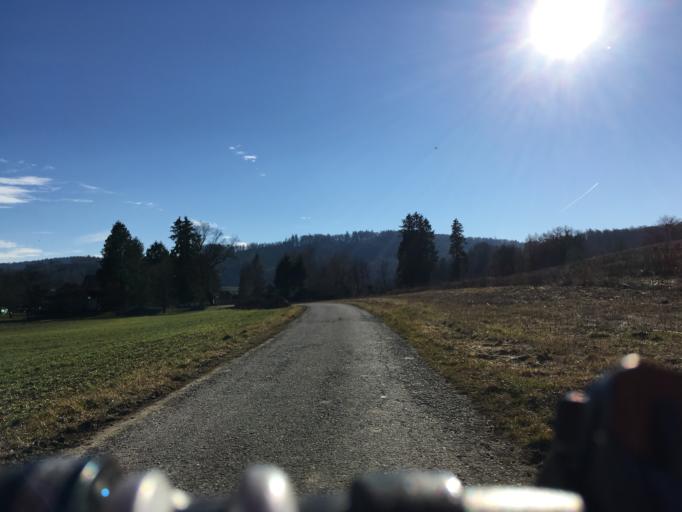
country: CH
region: Schaffhausen
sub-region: Bezirk Stein
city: Ramsen
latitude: 47.6828
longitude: 8.8049
